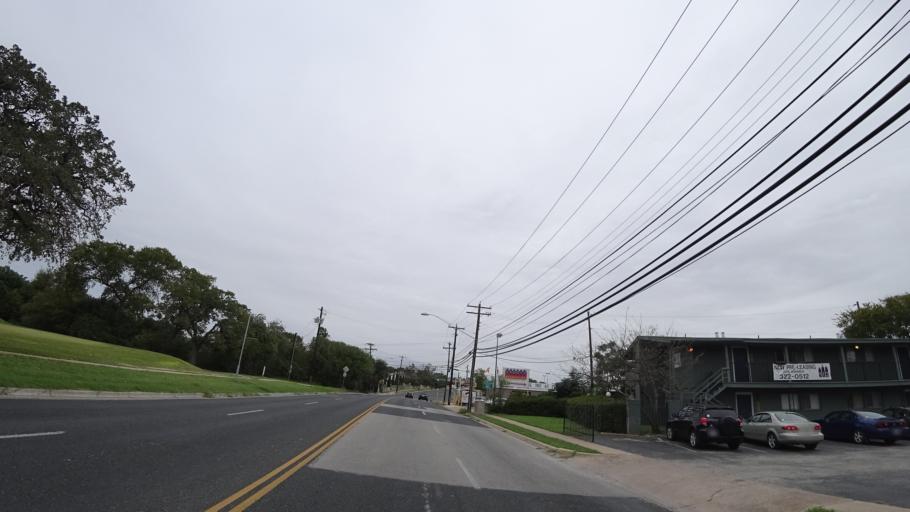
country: US
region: Texas
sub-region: Travis County
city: Austin
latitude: 30.2988
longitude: -97.7226
